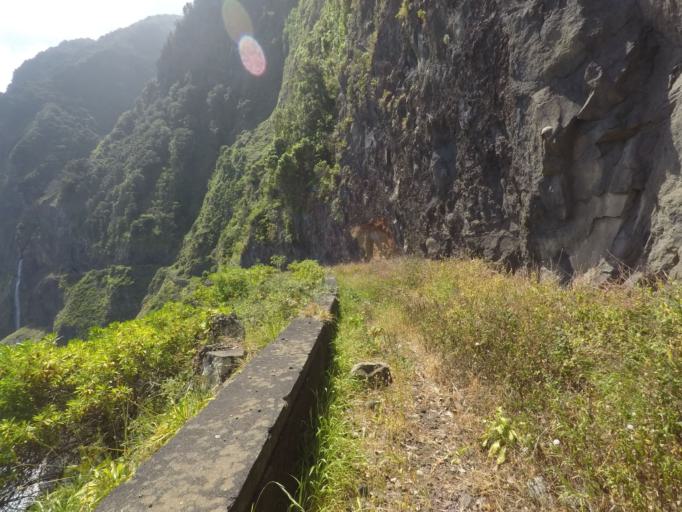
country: PT
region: Madeira
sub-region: Sao Vicente
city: Sao Vicente
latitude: 32.8156
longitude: -17.0947
